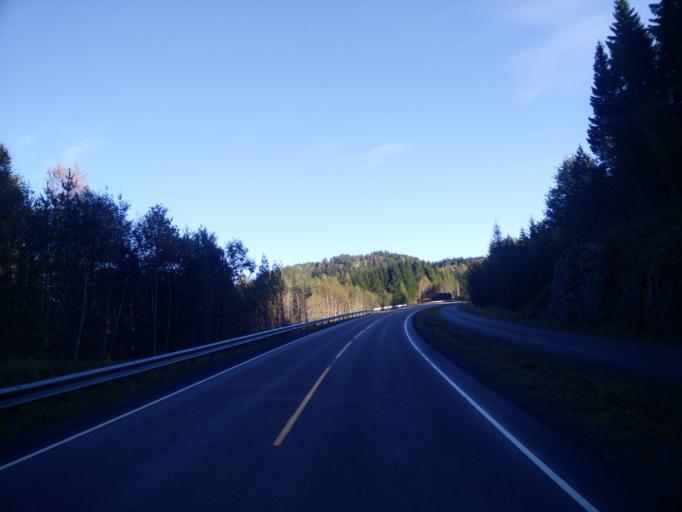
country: NO
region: More og Romsdal
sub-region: Kristiansund
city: Rensvik
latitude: 63.0123
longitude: 7.9944
